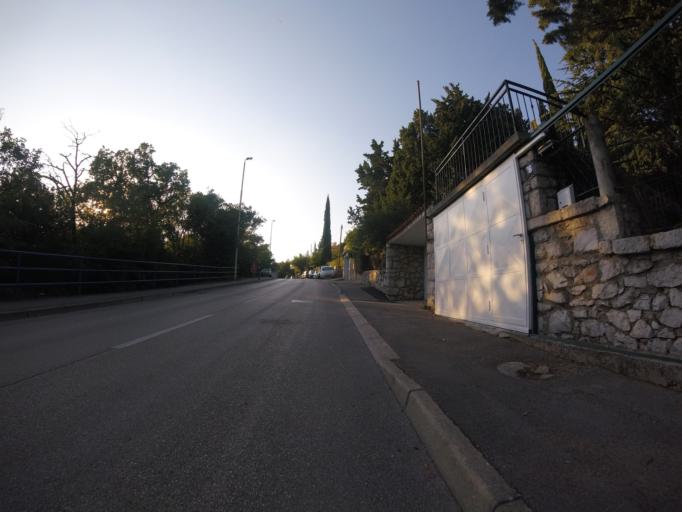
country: HR
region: Primorsko-Goranska
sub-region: Grad Crikvenica
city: Crikvenica
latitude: 45.1899
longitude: 14.6731
